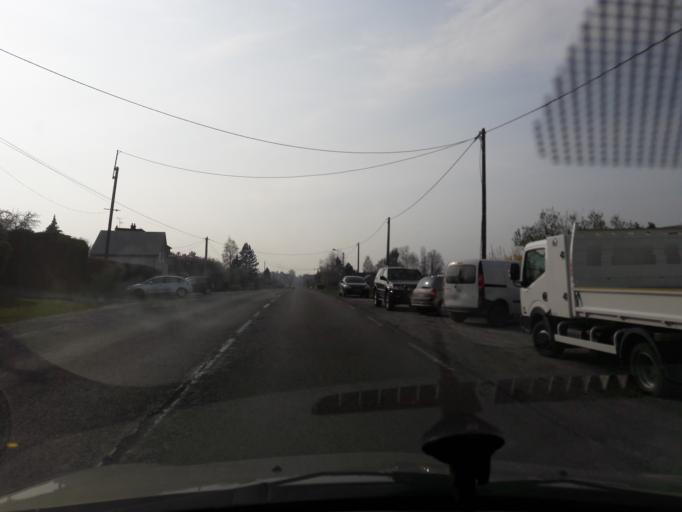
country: FR
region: Nord-Pas-de-Calais
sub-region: Departement du Nord
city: Marpent
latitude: 50.2526
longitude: 4.0869
